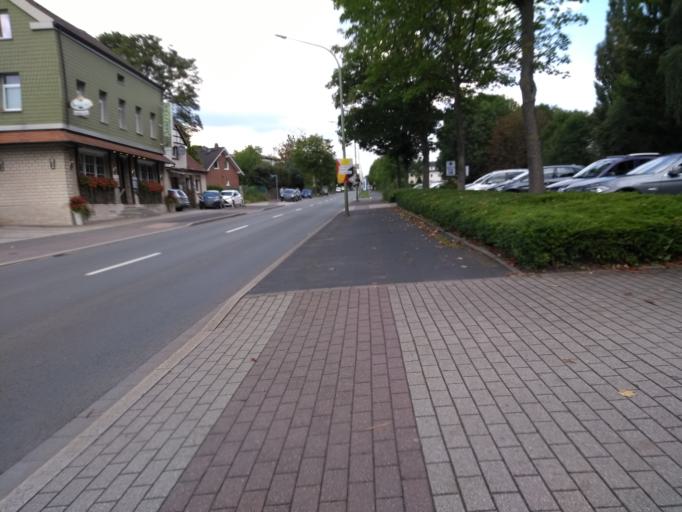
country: DE
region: North Rhine-Westphalia
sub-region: Regierungsbezirk Arnsberg
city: Hagen
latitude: 51.3885
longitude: 7.4631
